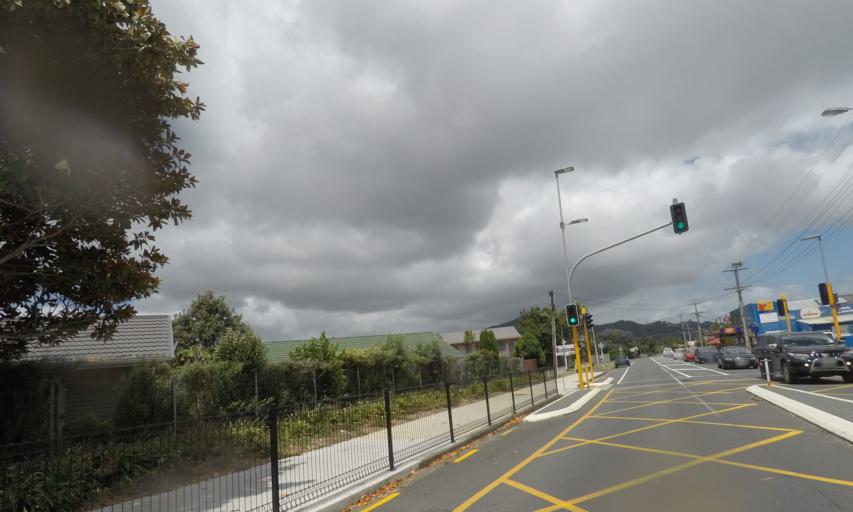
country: NZ
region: Northland
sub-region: Whangarei
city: Whangarei
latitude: -35.7039
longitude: 174.3174
